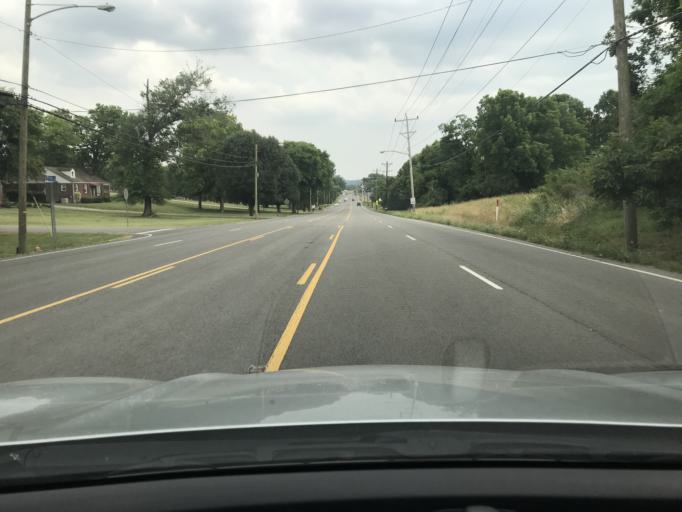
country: US
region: Tennessee
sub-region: Davidson County
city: Goodlettsville
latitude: 36.3093
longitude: -86.7167
